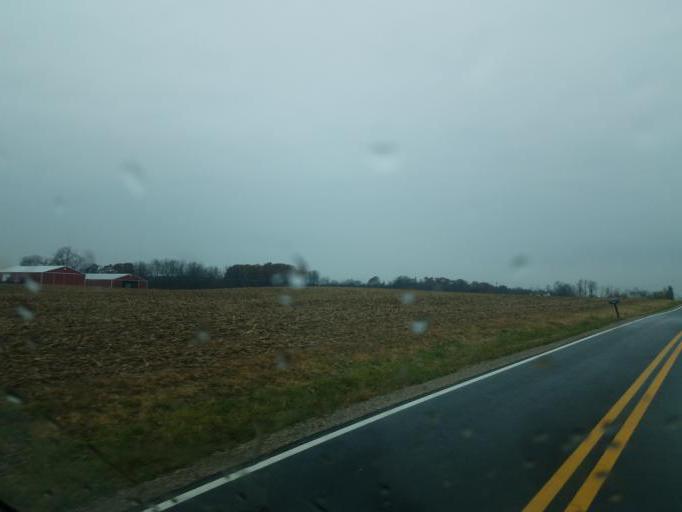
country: US
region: Ohio
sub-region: Knox County
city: Centerburg
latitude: 40.3194
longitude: -82.7592
